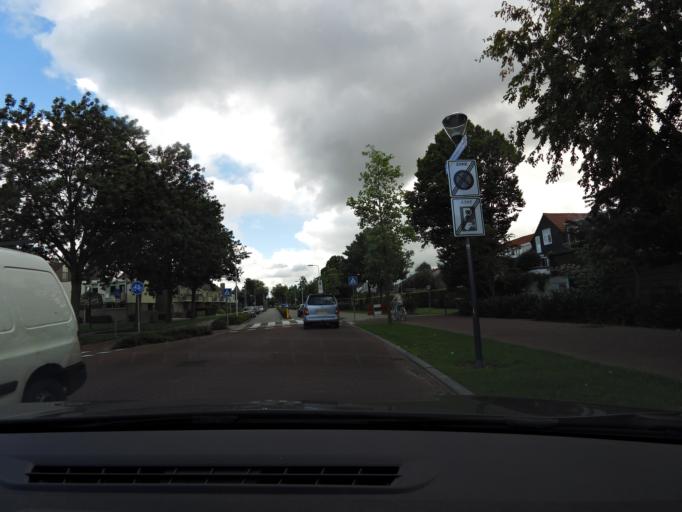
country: NL
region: South Holland
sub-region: Gemeente Oud-Beijerland
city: Oud-Beijerland
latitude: 51.8263
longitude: 4.4159
